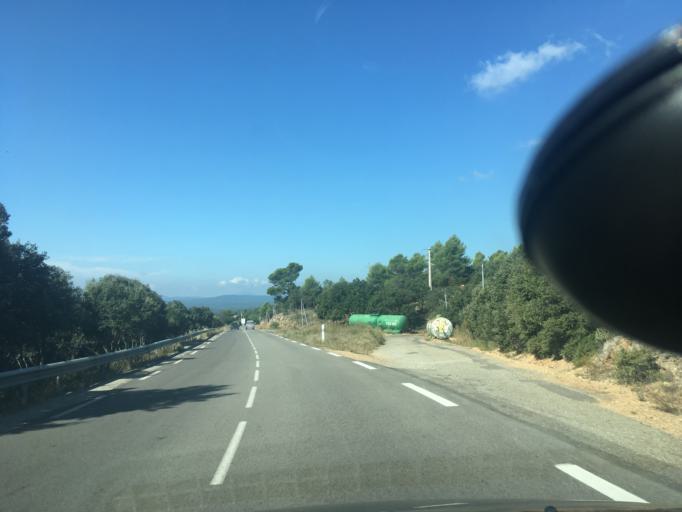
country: FR
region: Provence-Alpes-Cote d'Azur
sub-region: Departement du Var
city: Barjols
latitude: 43.6028
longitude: 6.0596
